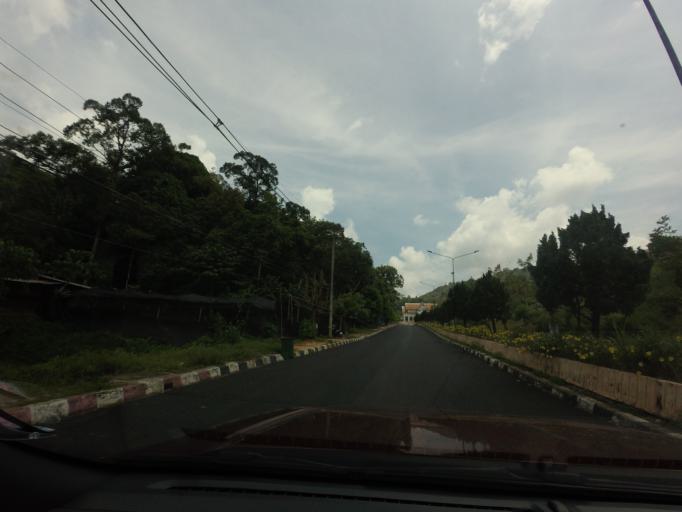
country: TH
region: Yala
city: Betong
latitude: 5.7476
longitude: 101.0342
